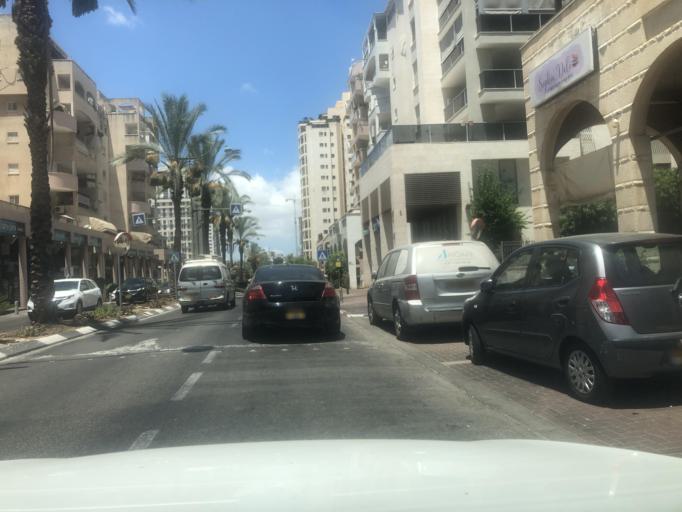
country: IL
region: Central District
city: Hod HaSharon
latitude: 32.1620
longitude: 34.9028
